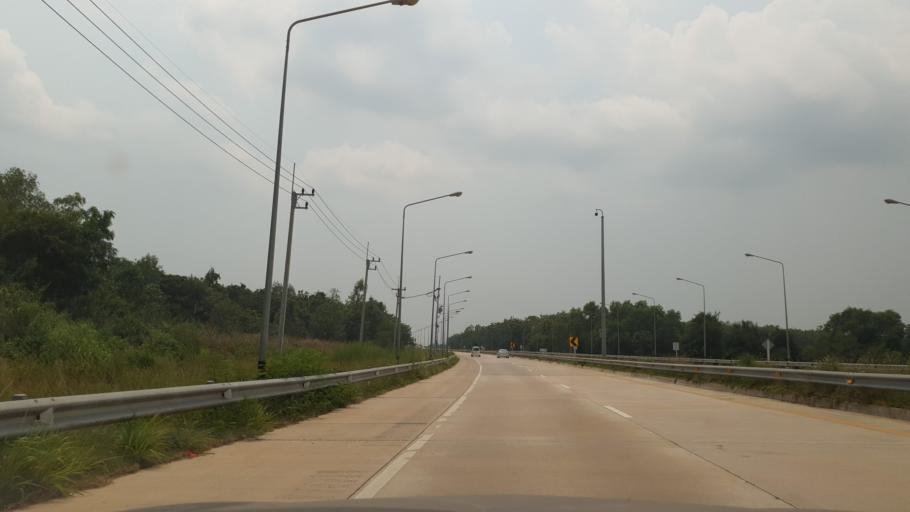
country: TH
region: Chon Buri
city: Phatthaya
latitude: 12.8401
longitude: 100.9558
